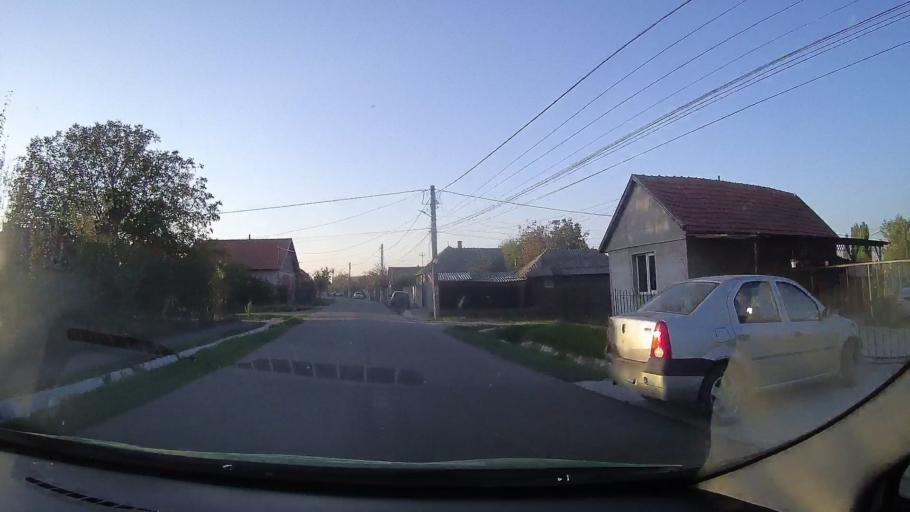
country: RO
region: Bihor
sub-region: Comuna Salard
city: Salard
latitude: 47.2217
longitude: 22.0368
